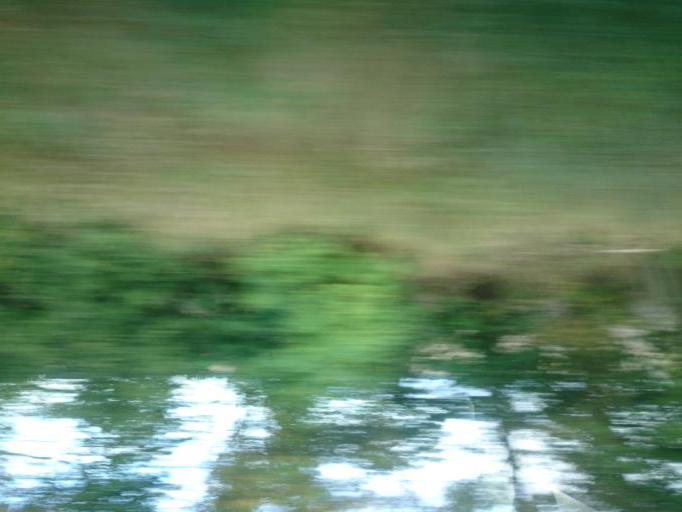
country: DE
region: Mecklenburg-Vorpommern
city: Ducherow
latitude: 53.8036
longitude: 13.7385
